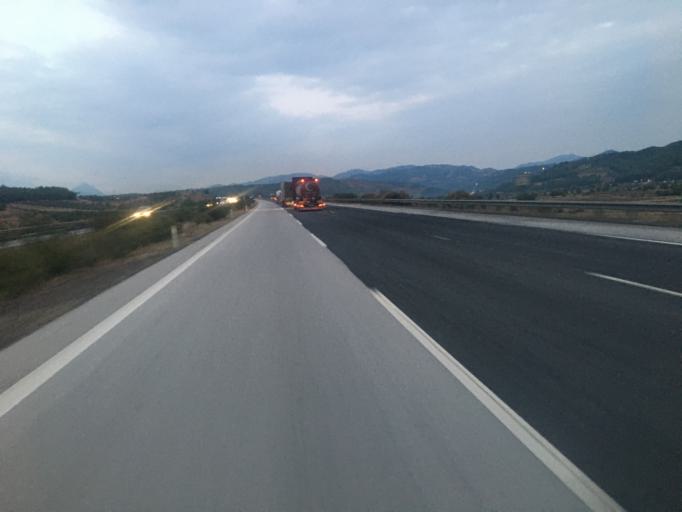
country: TR
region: Osmaniye
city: Kaypak
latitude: 37.1536
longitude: 36.3489
